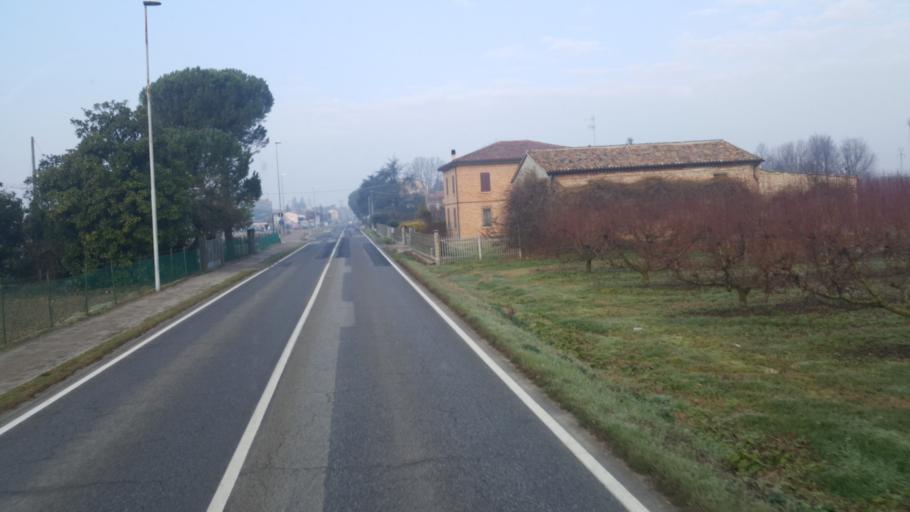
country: IT
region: Emilia-Romagna
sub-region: Provincia di Ravenna
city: Bagnacavallo
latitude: 44.4114
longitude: 11.9897
